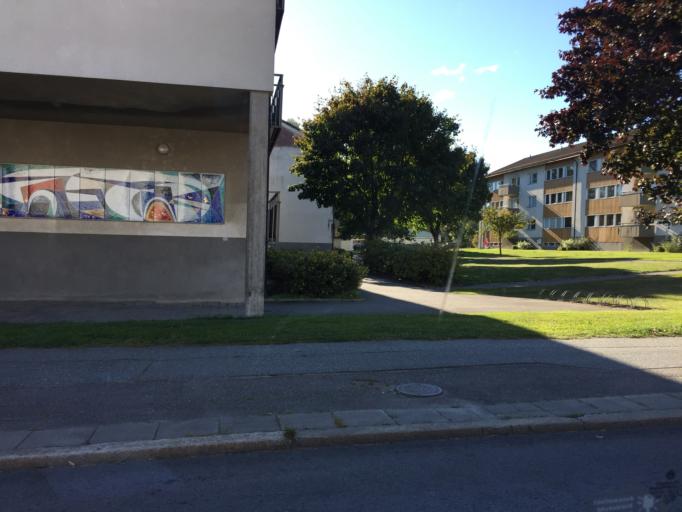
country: SE
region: OErebro
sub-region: Kumla Kommun
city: Kumla
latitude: 59.1246
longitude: 15.1429
